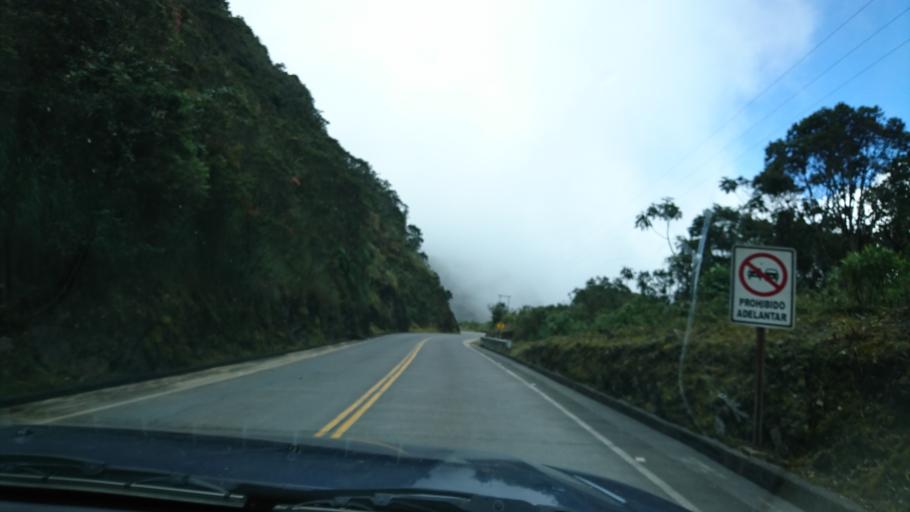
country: BO
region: La Paz
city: Coroico
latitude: -16.2869
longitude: -67.8348
